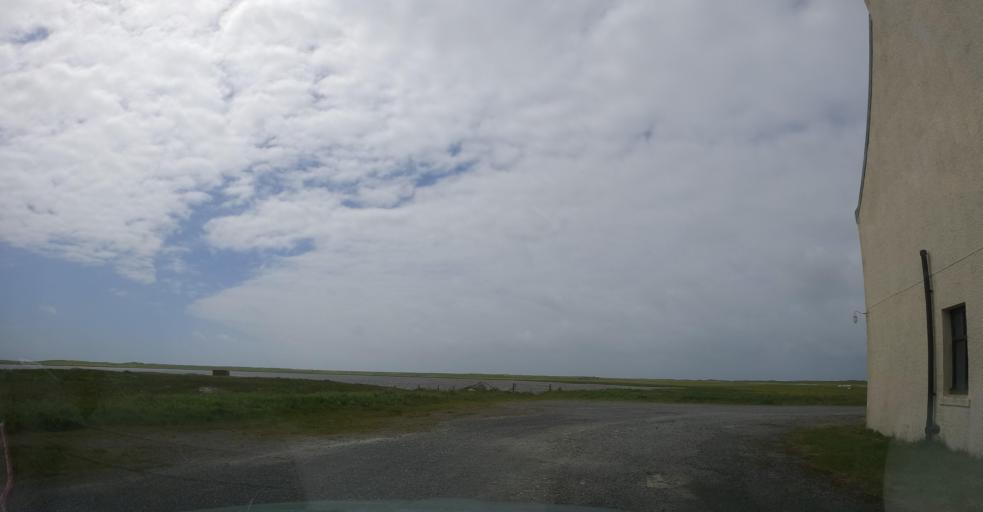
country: GB
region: Scotland
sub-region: Eilean Siar
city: Isle of South Uist
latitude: 57.2407
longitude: -7.4181
